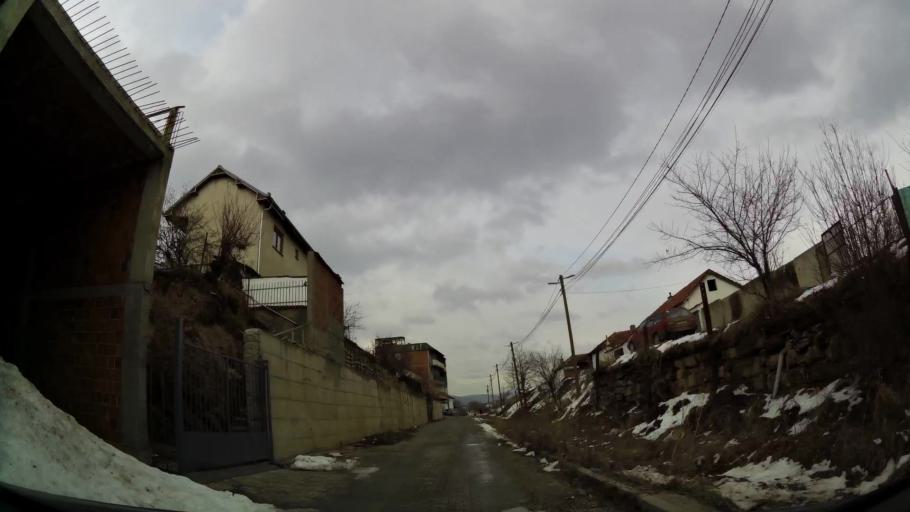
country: XK
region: Pristina
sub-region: Komuna e Prishtines
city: Pristina
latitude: 42.6768
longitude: 21.1697
